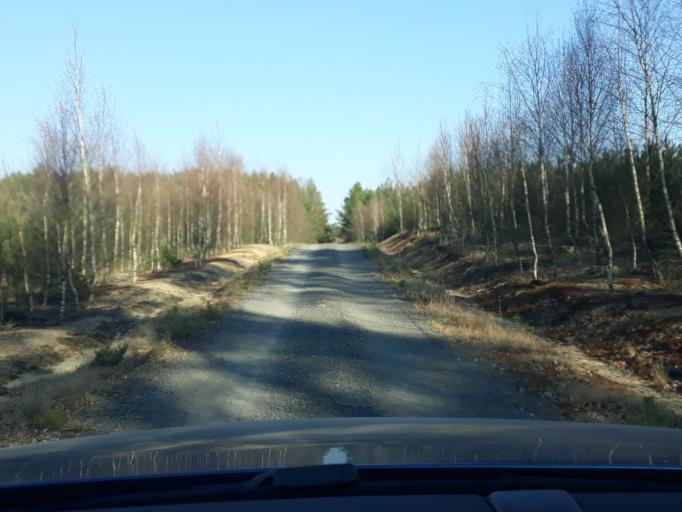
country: PL
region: Pomeranian Voivodeship
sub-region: Powiat bytowski
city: Lipnica
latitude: 53.9136
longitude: 17.4879
